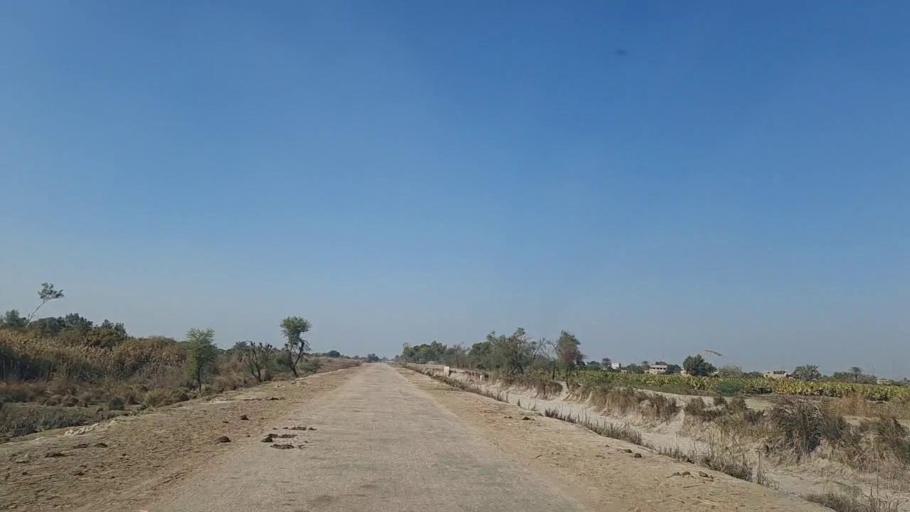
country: PK
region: Sindh
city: Shahpur Chakar
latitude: 26.2197
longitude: 68.6037
